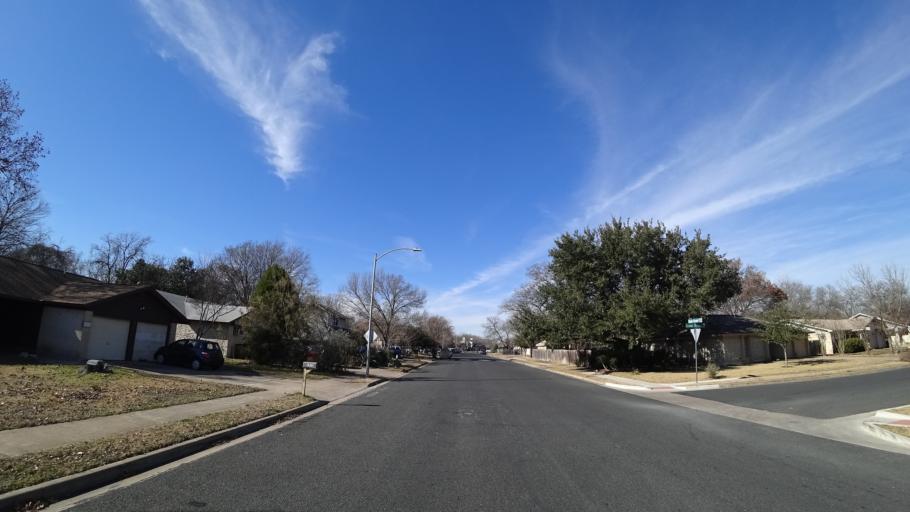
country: US
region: Texas
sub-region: Travis County
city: Wells Branch
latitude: 30.3800
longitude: -97.7078
